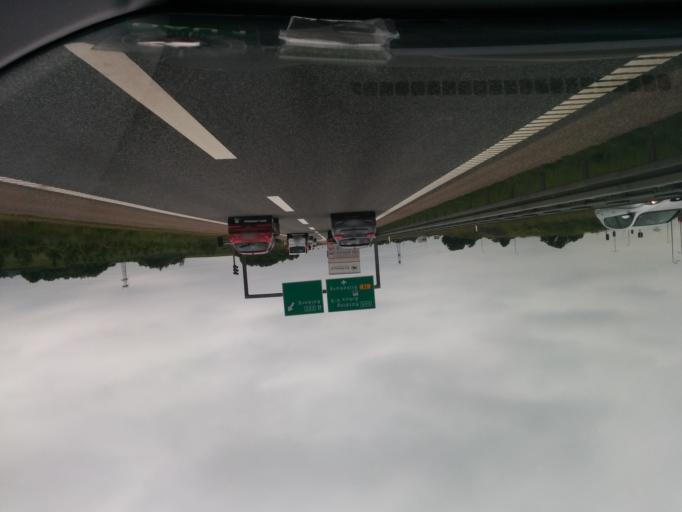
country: DK
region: Central Jutland
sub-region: Arhus Kommune
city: Trige
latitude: 56.2235
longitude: 10.1244
